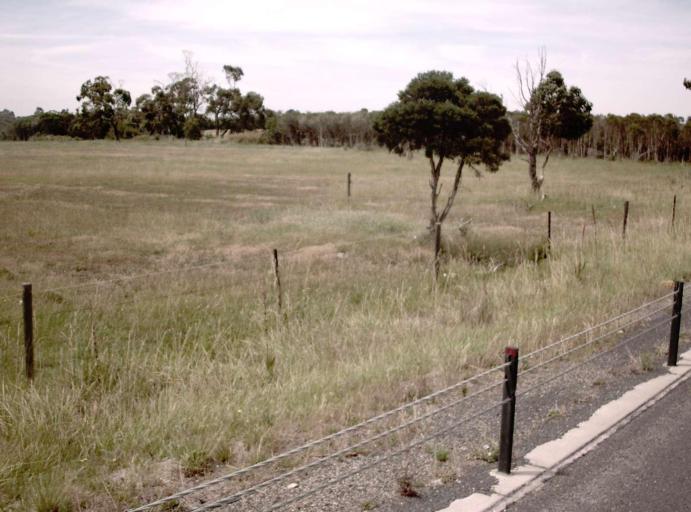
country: AU
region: Victoria
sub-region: Mornington Peninsula
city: Tyabb
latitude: -38.2319
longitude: 145.2162
